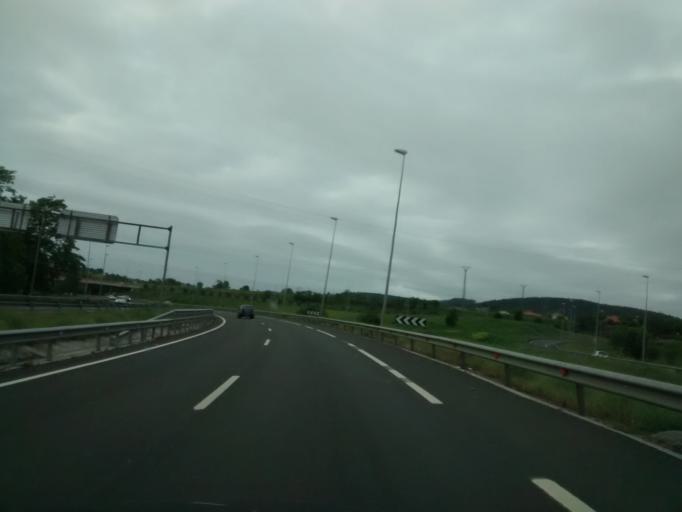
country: ES
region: Cantabria
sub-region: Provincia de Cantabria
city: Torrelavega
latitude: 43.3434
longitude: -4.0274
